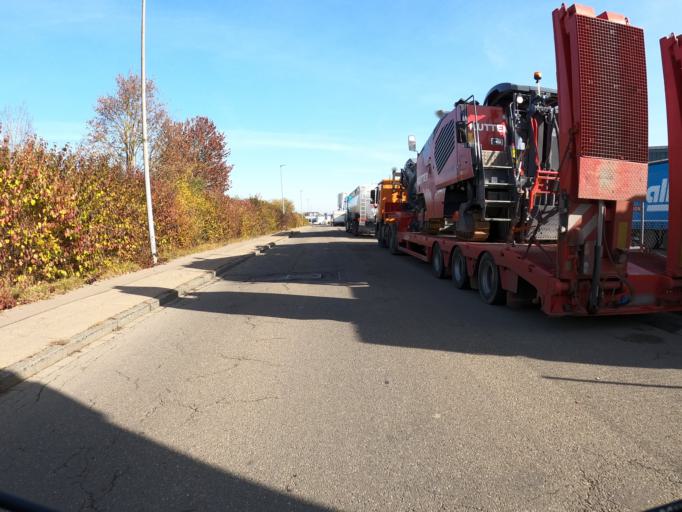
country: DE
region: Bavaria
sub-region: Swabia
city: Nersingen
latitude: 48.4529
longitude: 10.1050
